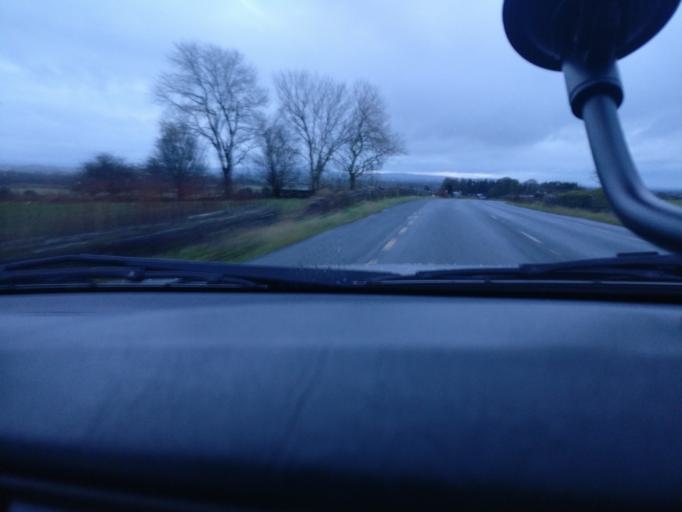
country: IE
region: Connaught
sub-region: County Galway
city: Loughrea
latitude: 53.2629
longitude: -8.4223
